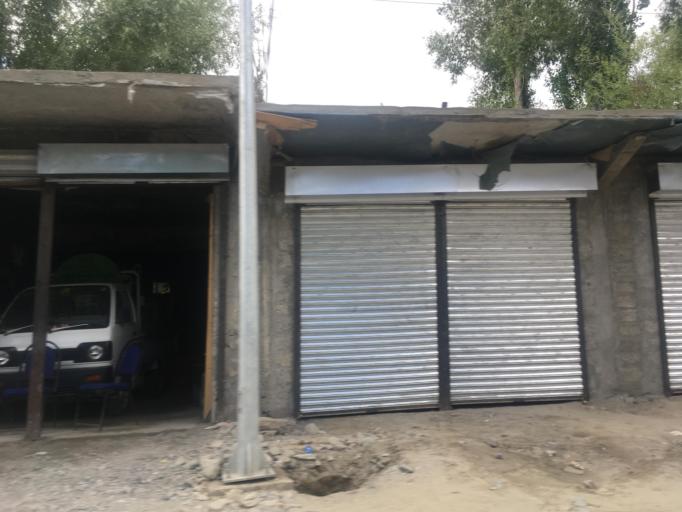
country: PK
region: Gilgit-Baltistan
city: Skardu
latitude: 35.2923
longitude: 75.6136
